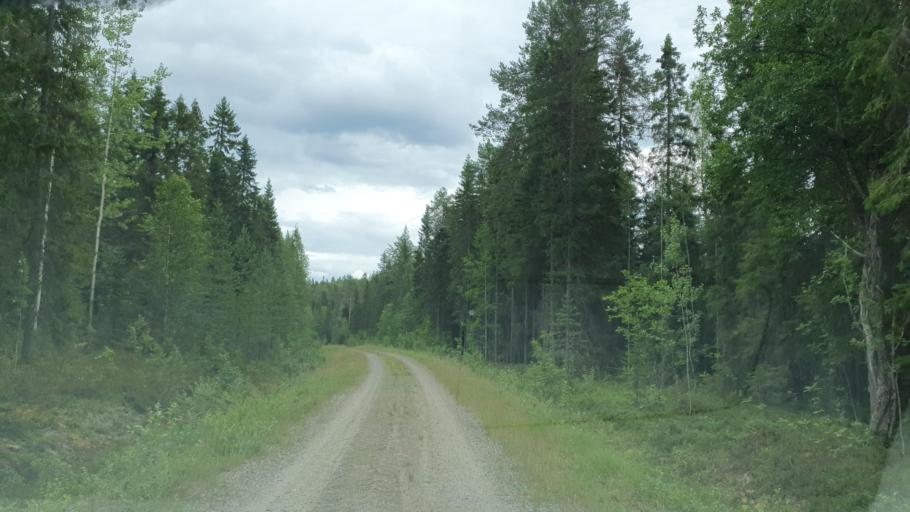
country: FI
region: Kainuu
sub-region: Kehys-Kainuu
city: Kuhmo
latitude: 64.2024
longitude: 29.3859
